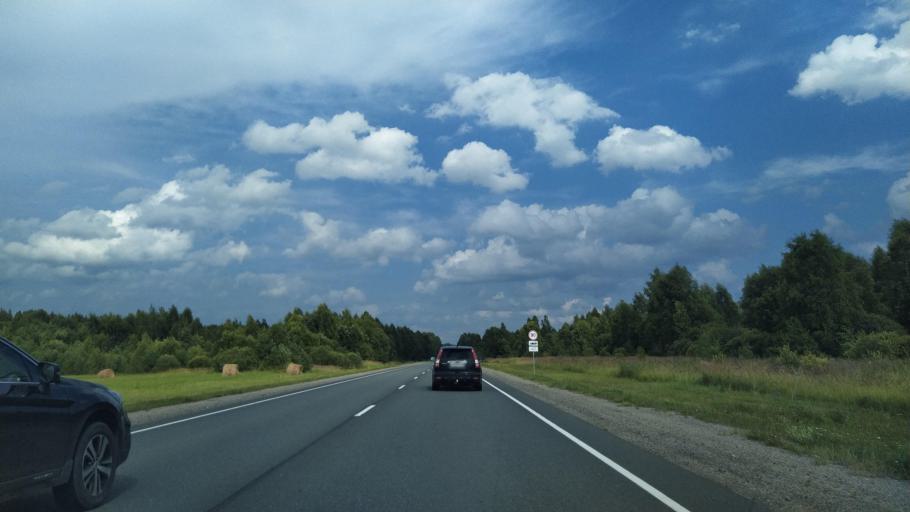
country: RU
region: Pskov
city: Porkhov
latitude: 57.8575
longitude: 29.5603
